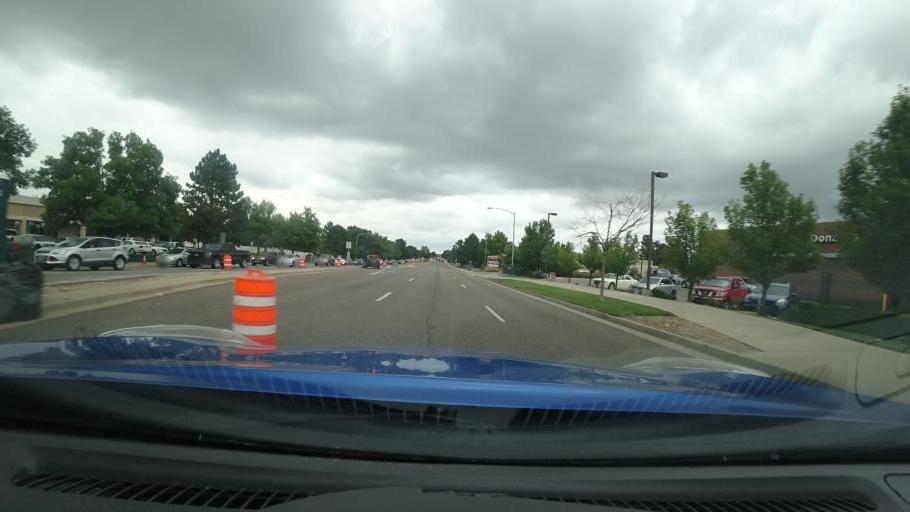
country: US
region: Colorado
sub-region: Adams County
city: Aurora
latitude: 39.6975
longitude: -104.8097
